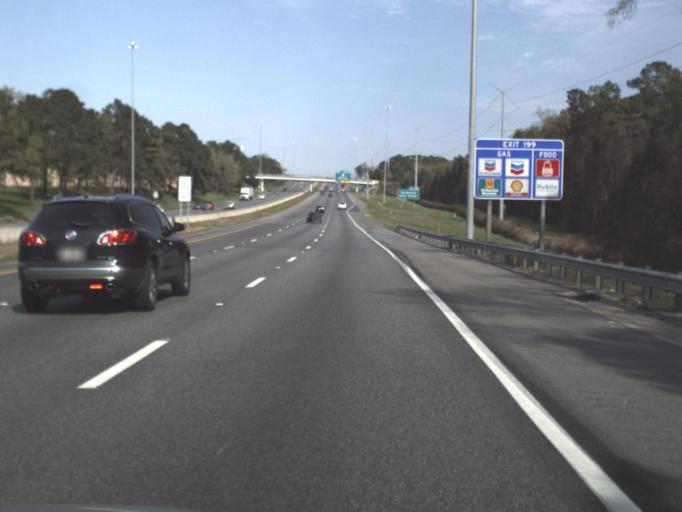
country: US
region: Florida
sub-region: Leon County
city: Tallahassee
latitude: 30.4791
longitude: -84.3234
